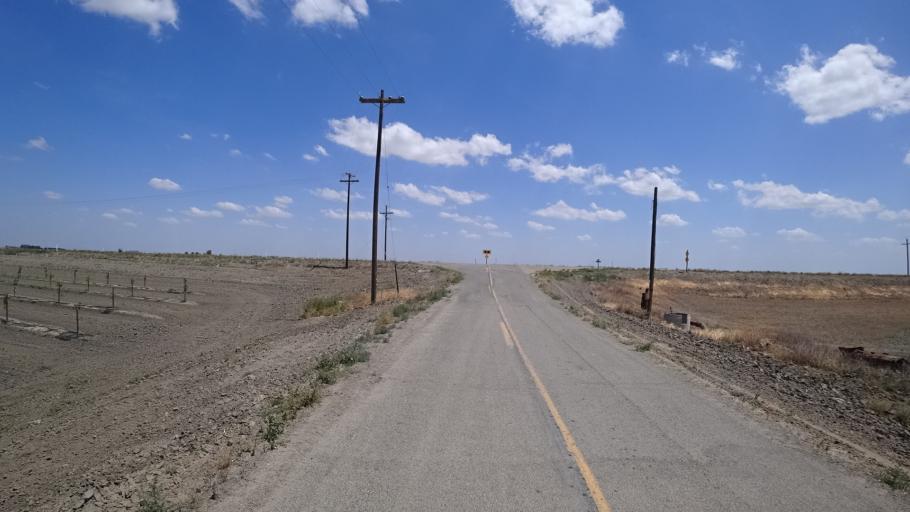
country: US
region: California
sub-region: Kings County
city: Stratford
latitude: 36.1526
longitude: -119.7988
